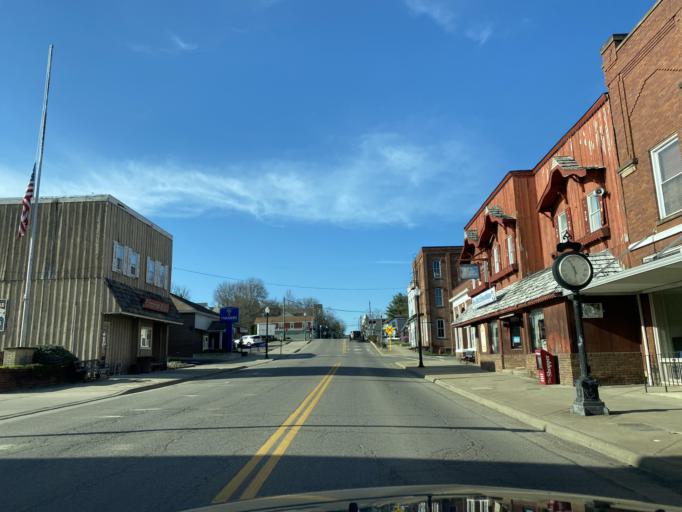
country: US
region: Ohio
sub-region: Wayne County
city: Shreve
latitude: 40.6817
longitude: -82.0223
